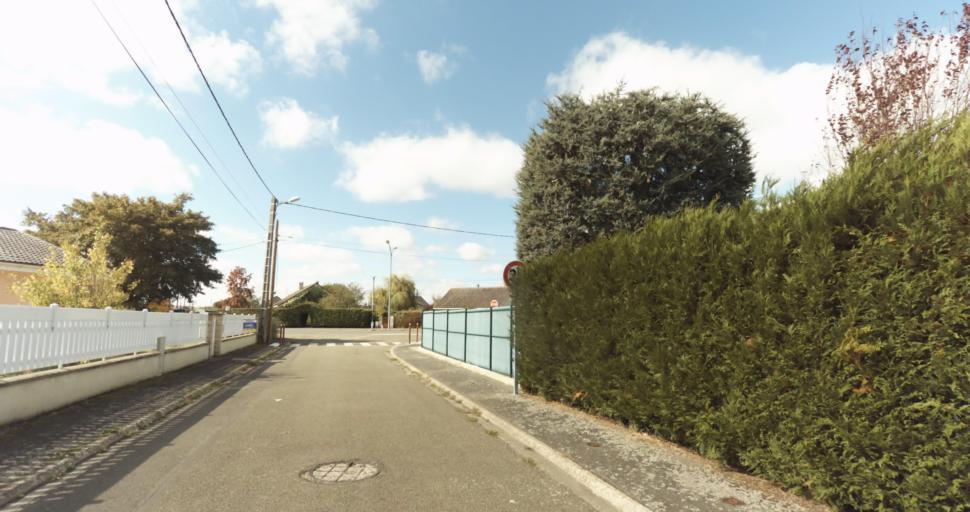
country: FR
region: Centre
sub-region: Departement d'Eure-et-Loir
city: Garnay
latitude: 48.7319
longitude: 1.3303
